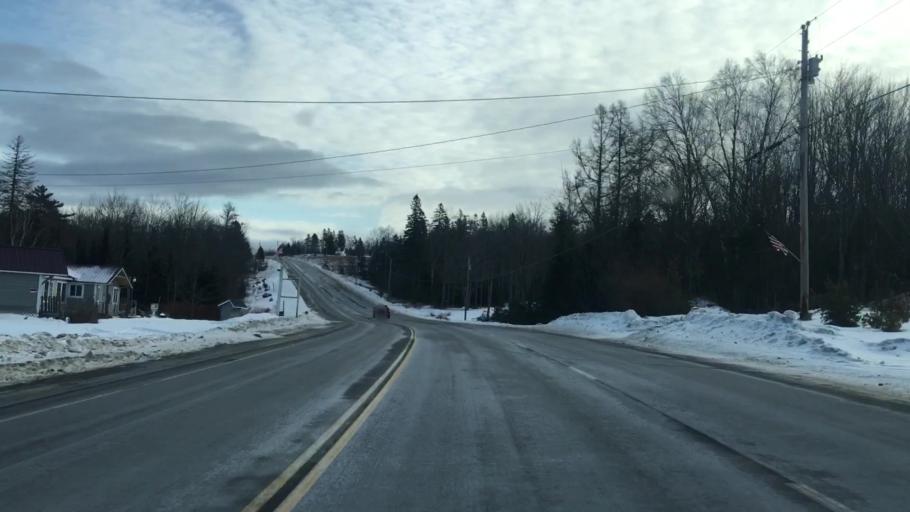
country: US
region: Maine
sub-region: Washington County
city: Machias
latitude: 44.9502
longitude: -67.6708
